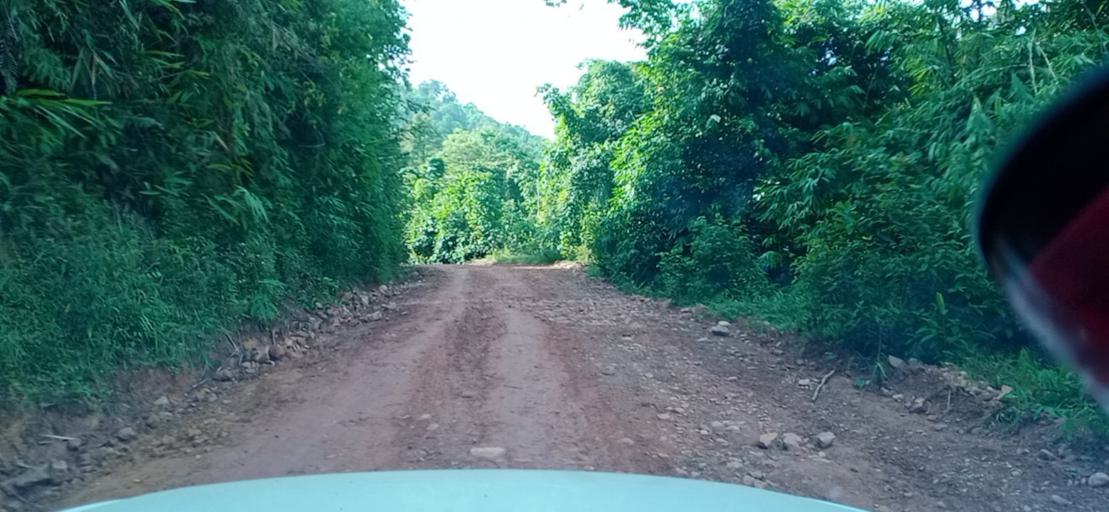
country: TH
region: Changwat Bueng Kan
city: Pak Khat
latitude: 18.6655
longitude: 103.1982
